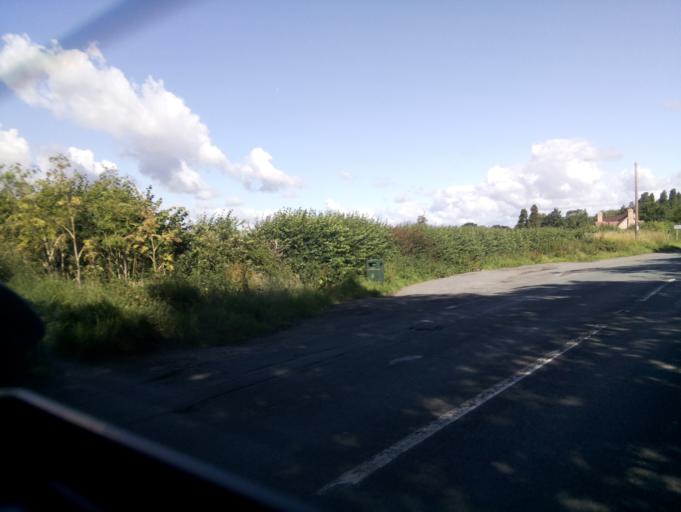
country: GB
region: England
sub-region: Herefordshire
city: Yatton
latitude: 51.9577
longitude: -2.5415
